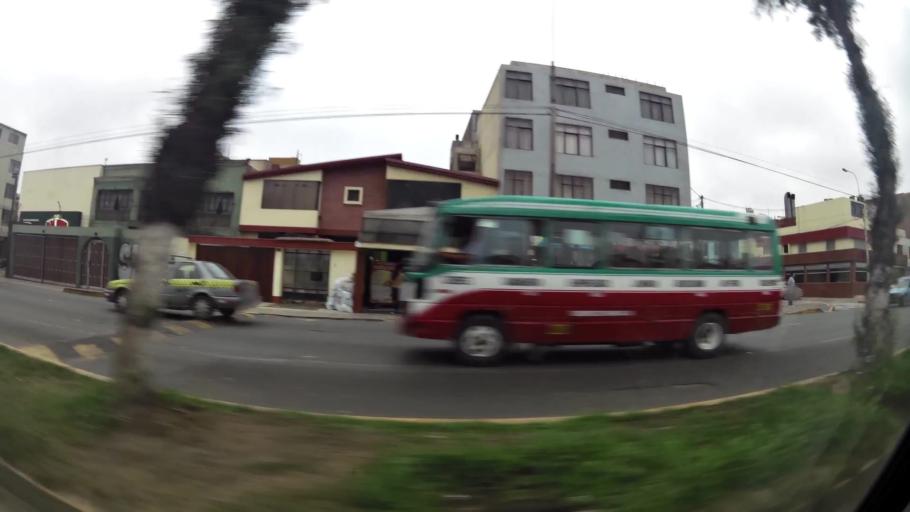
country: PE
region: Callao
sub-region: Callao
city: Callao
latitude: -12.0718
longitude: -77.0721
